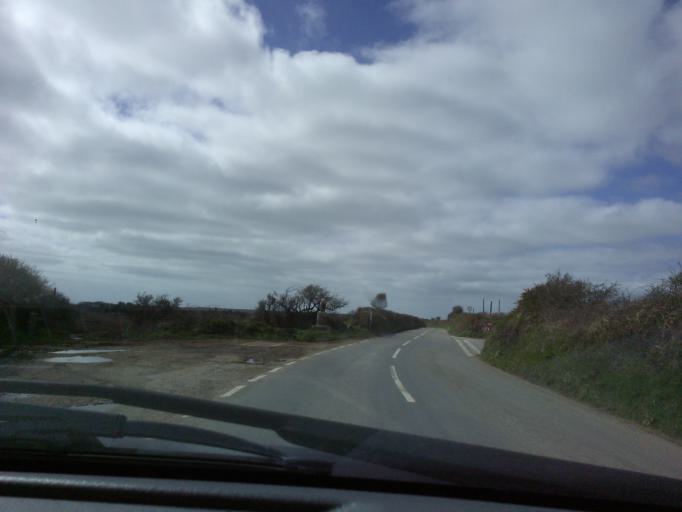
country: GB
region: England
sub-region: Cornwall
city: St. Buryan
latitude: 50.0628
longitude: -5.5977
